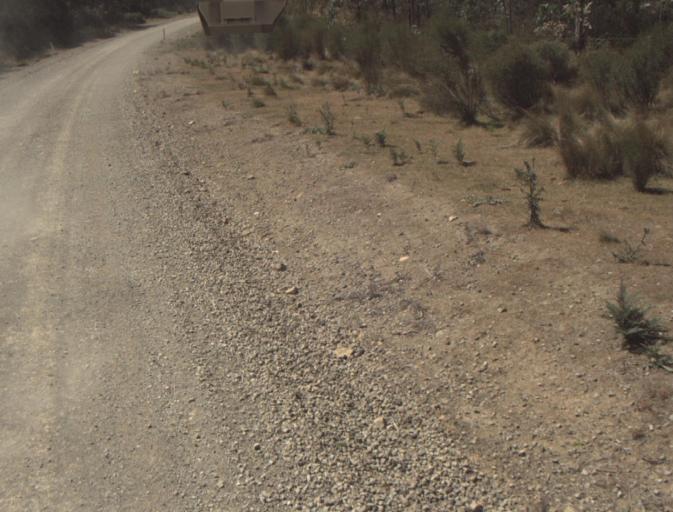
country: AU
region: Tasmania
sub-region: Dorset
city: Scottsdale
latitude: -41.3050
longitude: 147.4673
